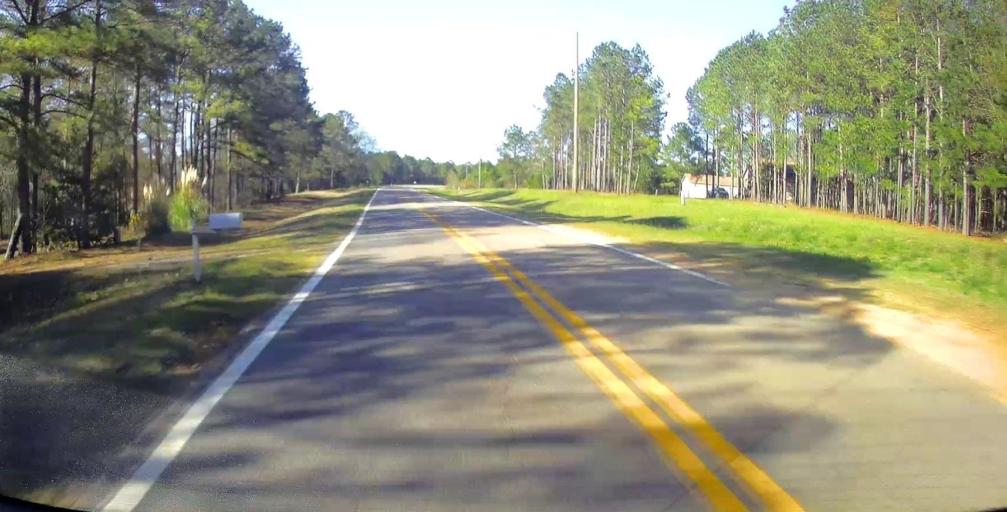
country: US
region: Georgia
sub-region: Peach County
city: Fort Valley
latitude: 32.5876
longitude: -83.9897
